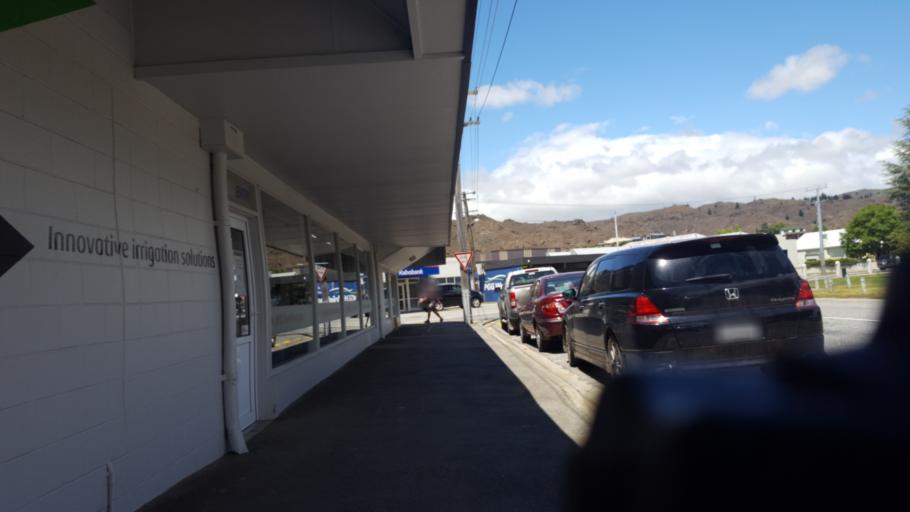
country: NZ
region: Otago
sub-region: Queenstown-Lakes District
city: Wanaka
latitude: -45.2531
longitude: 169.3940
